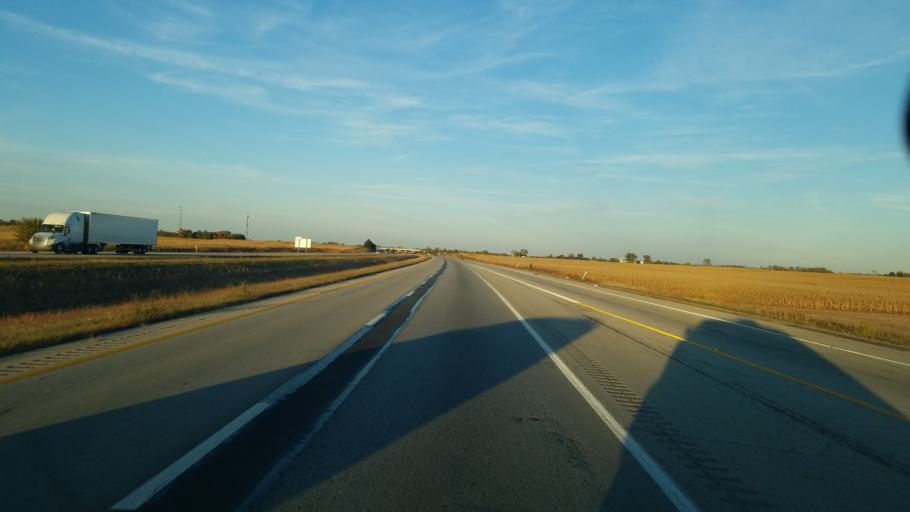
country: US
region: Ohio
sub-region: Greene County
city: Jamestown
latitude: 39.5585
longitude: -83.7166
